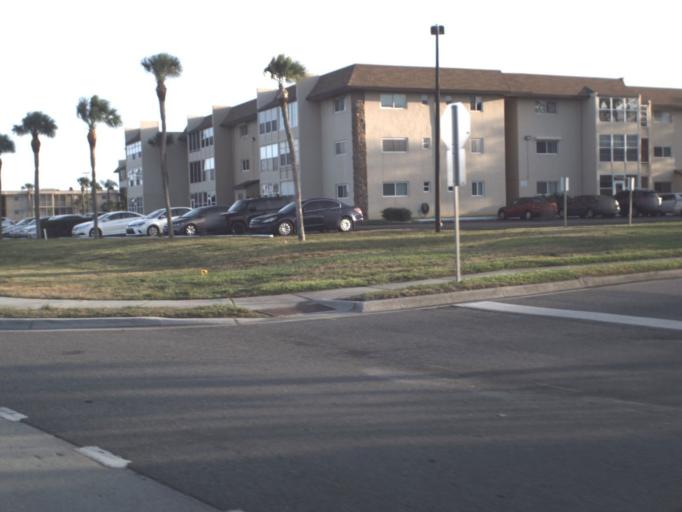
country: US
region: Florida
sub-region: Brevard County
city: South Patrick Shores
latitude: 28.1604
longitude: -80.6420
